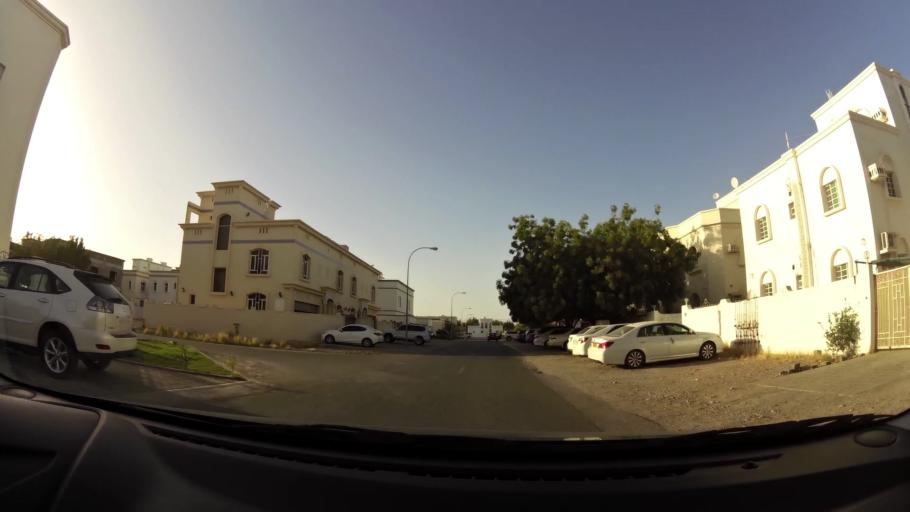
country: OM
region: Muhafazat Masqat
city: As Sib al Jadidah
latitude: 23.6111
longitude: 58.2292
